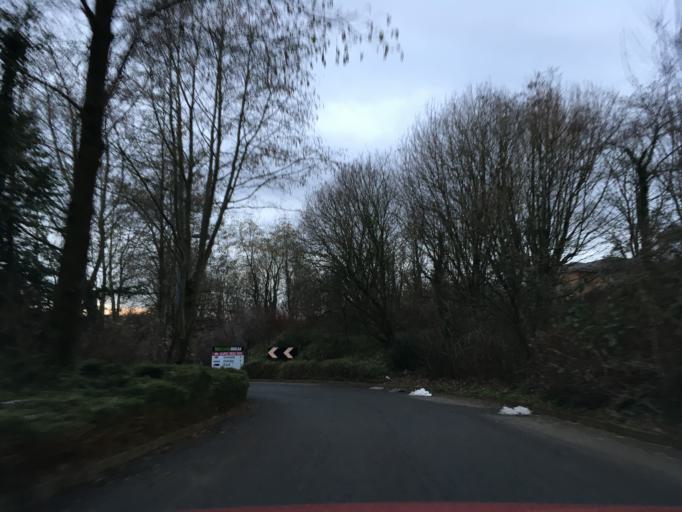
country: GB
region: Wales
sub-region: Caerphilly County Borough
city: Machen
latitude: 51.5401
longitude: -3.1307
